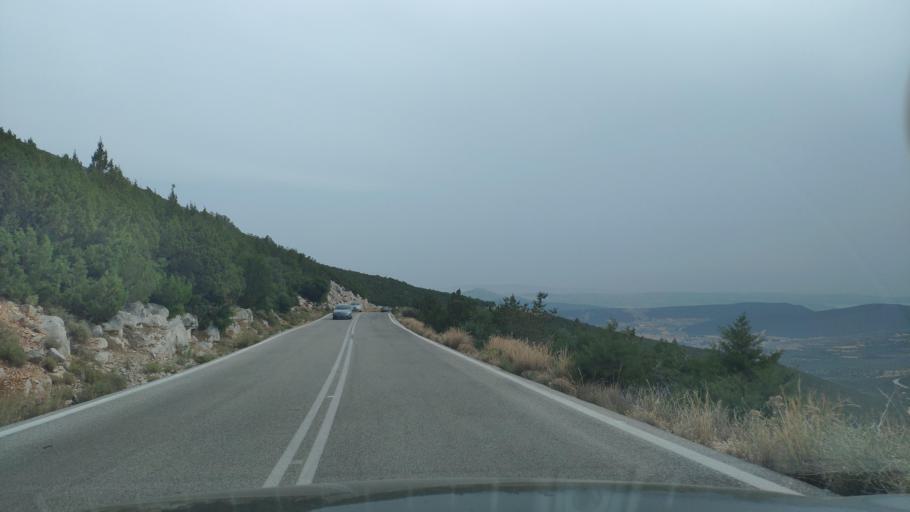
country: GR
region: Peloponnese
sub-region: Nomos Argolidos
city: Didyma
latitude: 37.4944
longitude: 23.1917
